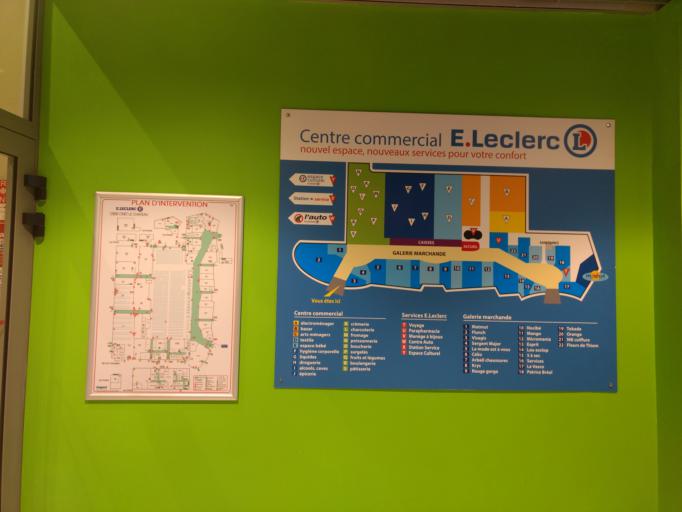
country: FR
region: Midi-Pyrenees
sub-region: Departement de l'Aveyron
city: Sebazac-Concoures
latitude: 44.3929
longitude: 2.6025
